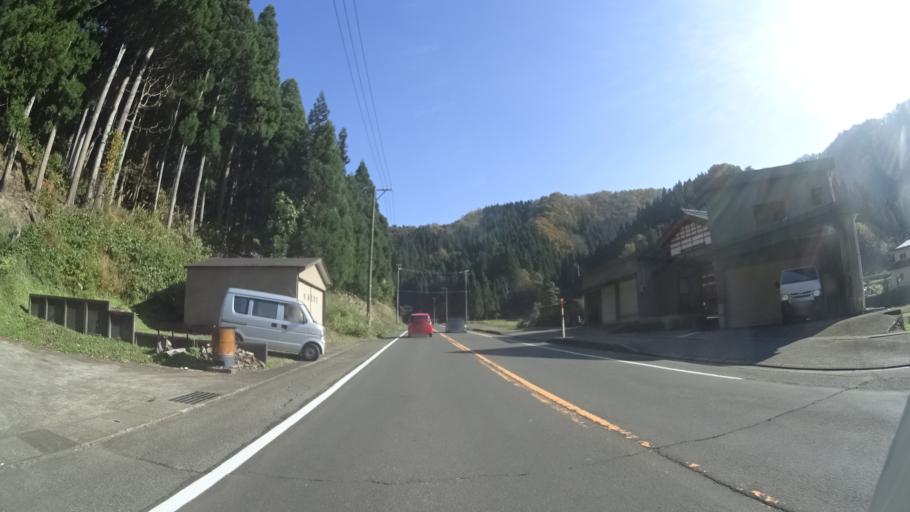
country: JP
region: Fukui
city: Ono
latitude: 35.9927
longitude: 136.4485
